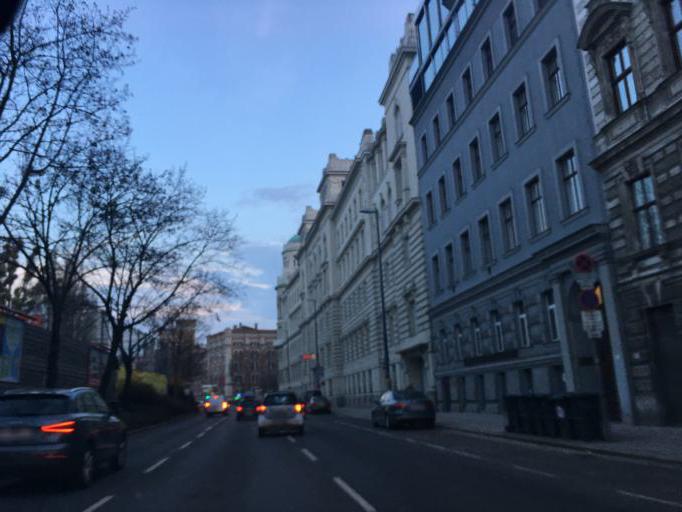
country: AT
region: Vienna
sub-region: Wien Stadt
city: Vienna
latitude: 48.2209
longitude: 16.3675
